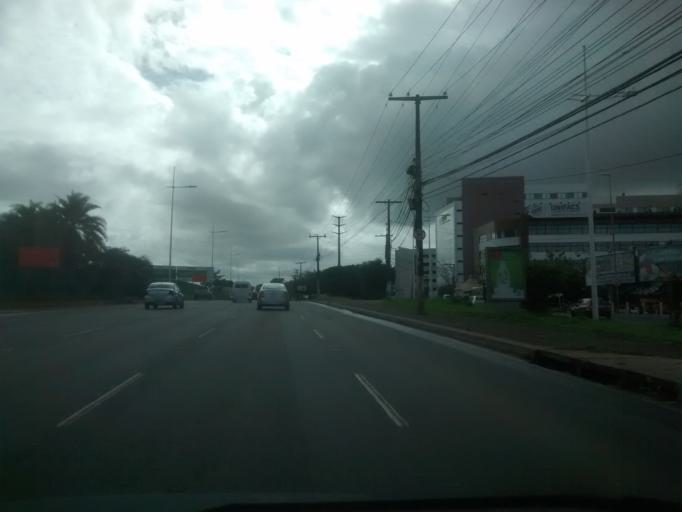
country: BR
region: Bahia
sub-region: Salvador
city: Salvador
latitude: -12.9619
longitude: -38.4334
